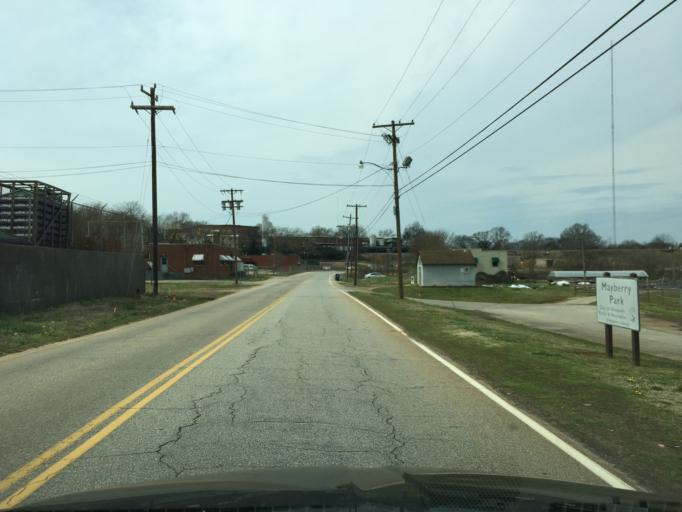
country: US
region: South Carolina
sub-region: Greenville County
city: City View
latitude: 34.8508
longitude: -82.4145
